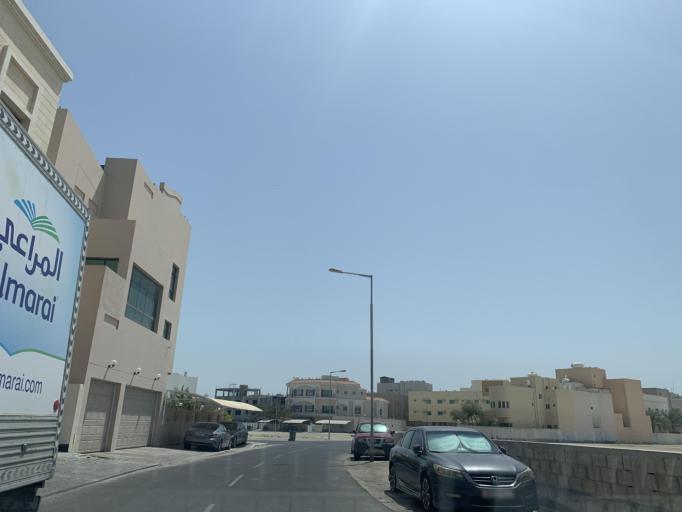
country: BH
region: Muharraq
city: Al Muharraq
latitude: 26.2799
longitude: 50.6066
